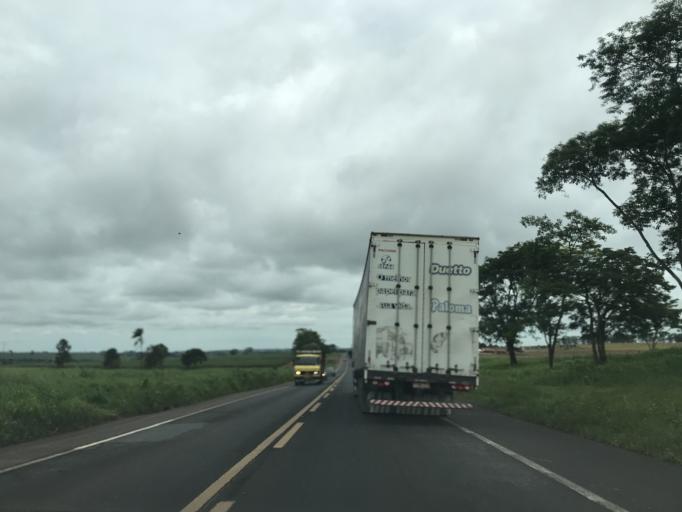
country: BR
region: Sao Paulo
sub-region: Nova Granada
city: Nova Granada
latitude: -20.4527
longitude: -49.2851
